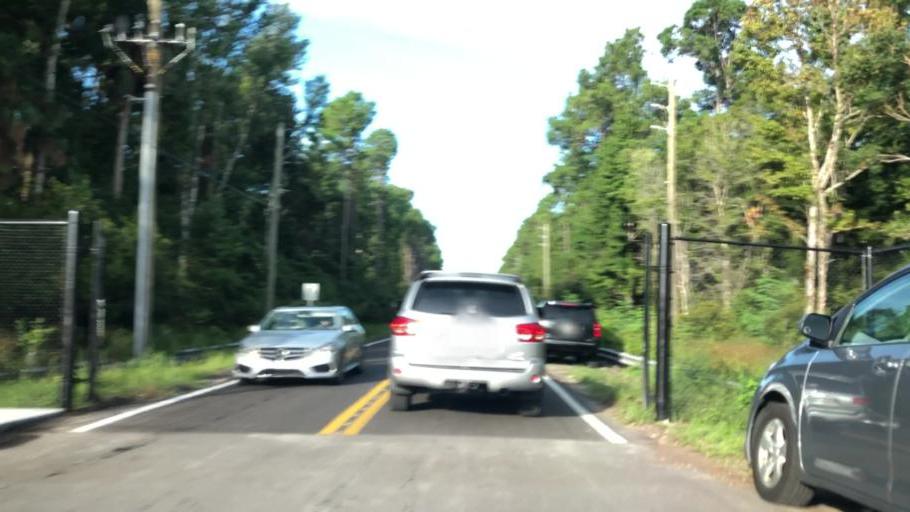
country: US
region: Florida
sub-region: Saint Johns County
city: Palm Valley
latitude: 30.1198
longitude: -81.4097
